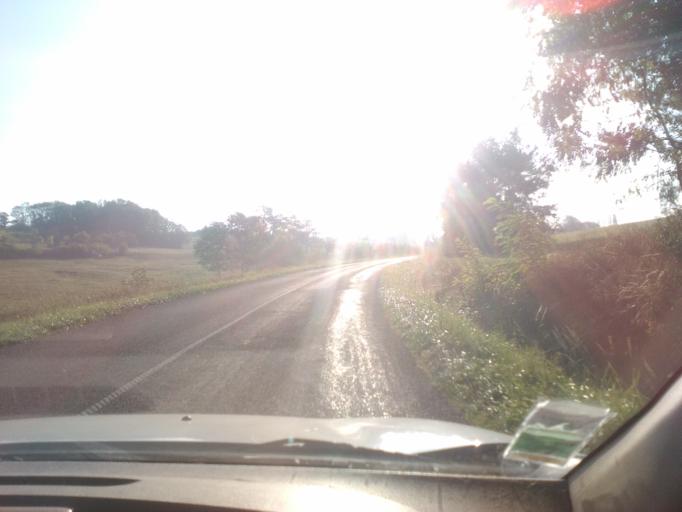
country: FR
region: Lorraine
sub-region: Departement des Vosges
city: Mirecourt
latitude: 48.3053
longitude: 6.1594
